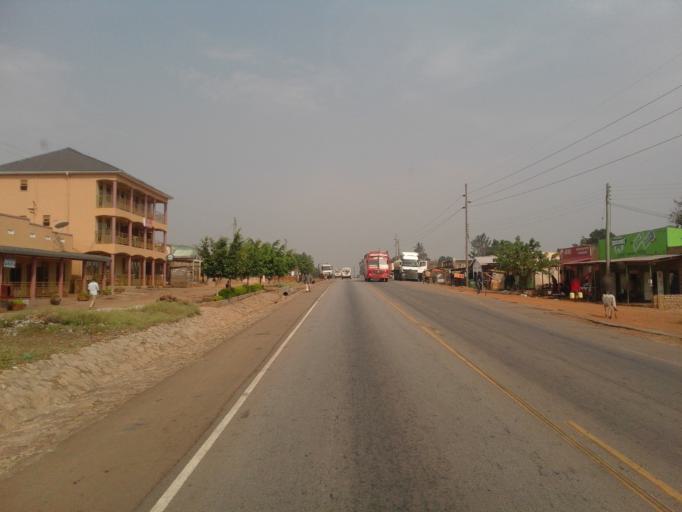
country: UG
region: Eastern Region
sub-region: Bugiri District
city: Bugiri
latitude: 0.5536
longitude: 33.7664
